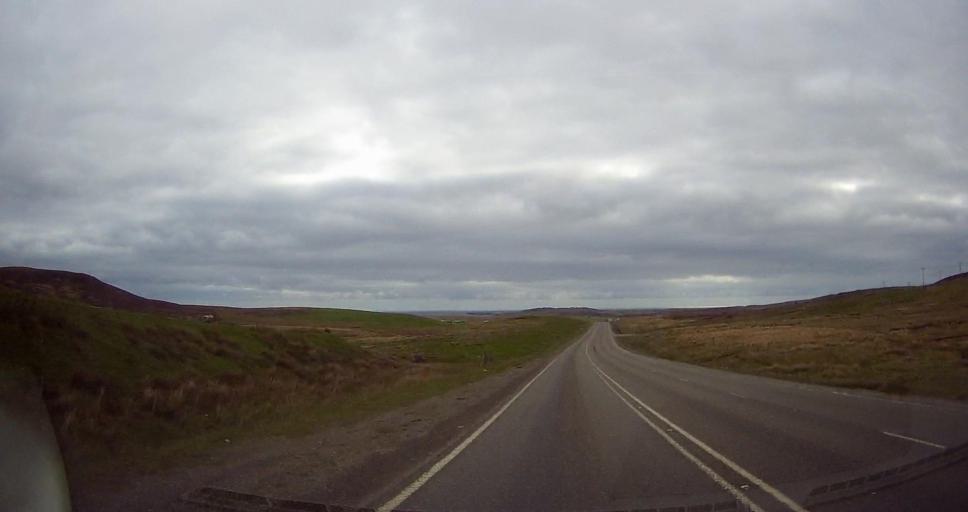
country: GB
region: Scotland
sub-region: Shetland Islands
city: Lerwick
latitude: 60.1688
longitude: -1.1886
